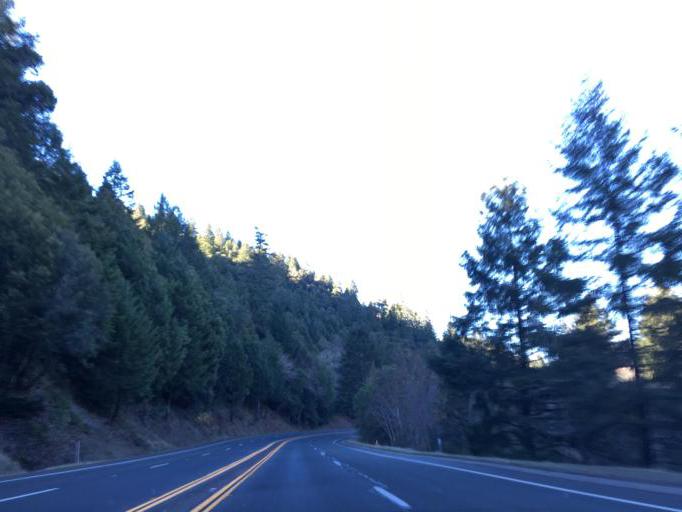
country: US
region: California
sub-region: Mendocino County
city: Brooktrails
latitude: 39.5435
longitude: -123.4228
